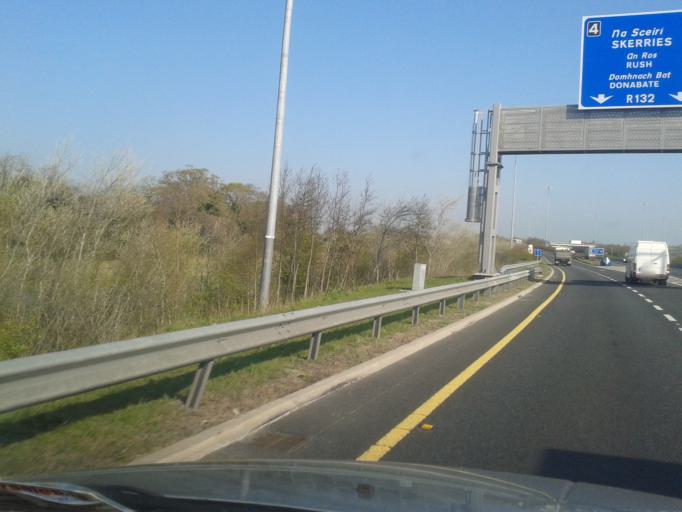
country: IE
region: Leinster
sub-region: Fingal County
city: Swords
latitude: 53.4728
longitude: -6.2032
